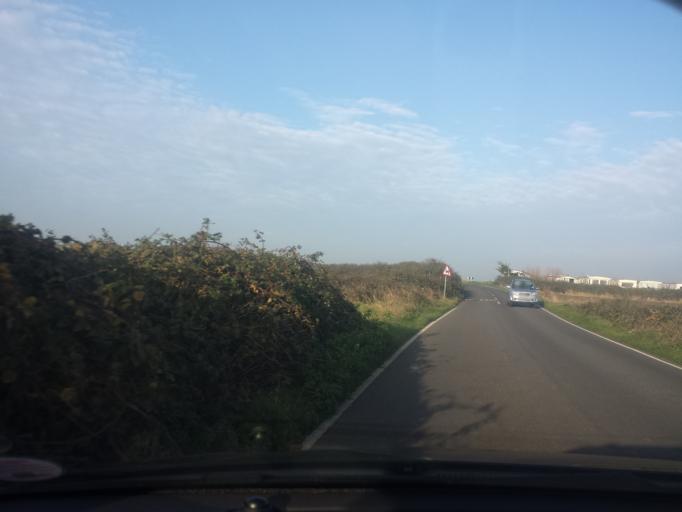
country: GB
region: England
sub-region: Essex
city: Saint Osyth
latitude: 51.7810
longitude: 1.0884
